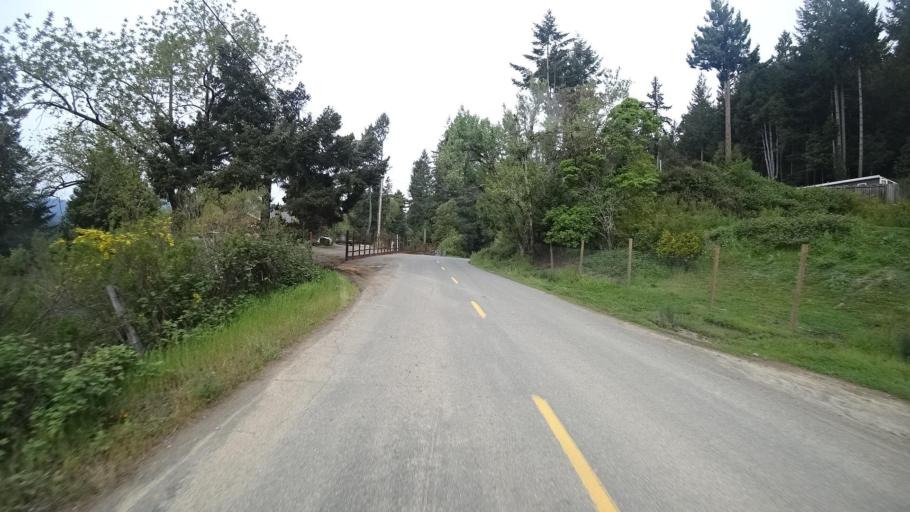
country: US
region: California
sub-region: Humboldt County
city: Redway
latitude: 40.2957
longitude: -123.8264
